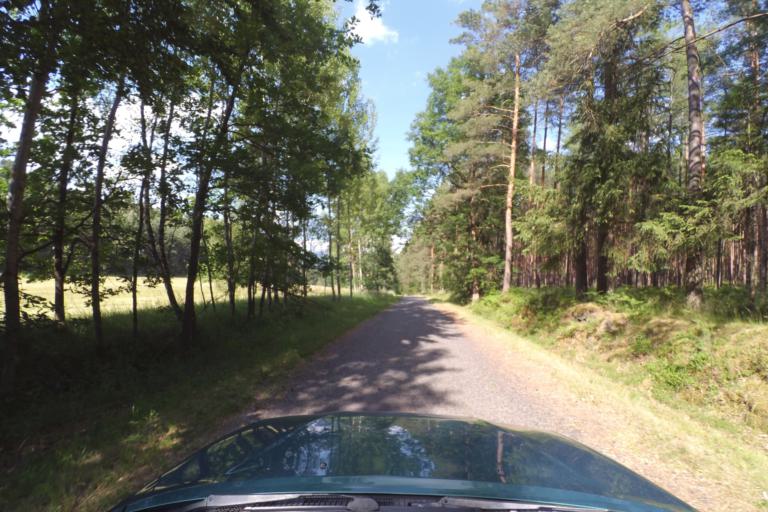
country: CZ
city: Osecna
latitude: 50.6855
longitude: 14.9065
